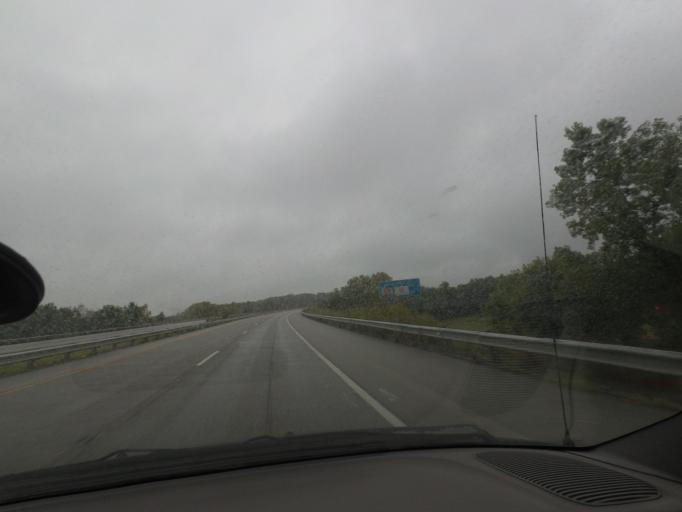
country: US
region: Illinois
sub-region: Pike County
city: Barry
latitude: 39.7165
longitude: -91.0695
